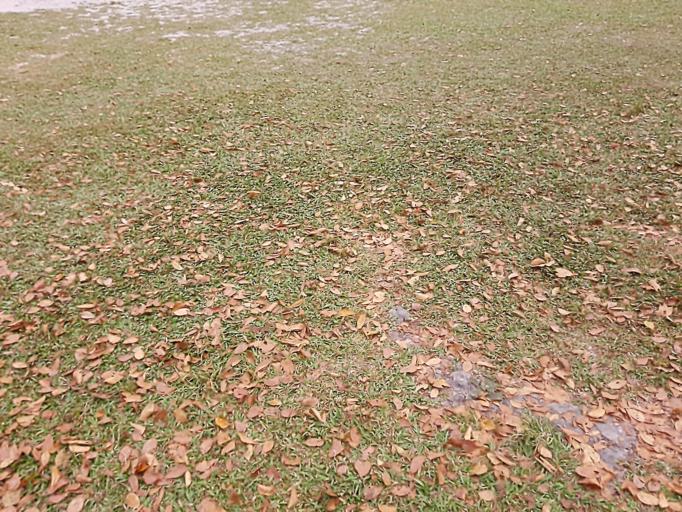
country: GT
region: Peten
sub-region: Municipio de San Jose
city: San Jose
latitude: 17.2220
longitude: -89.6236
